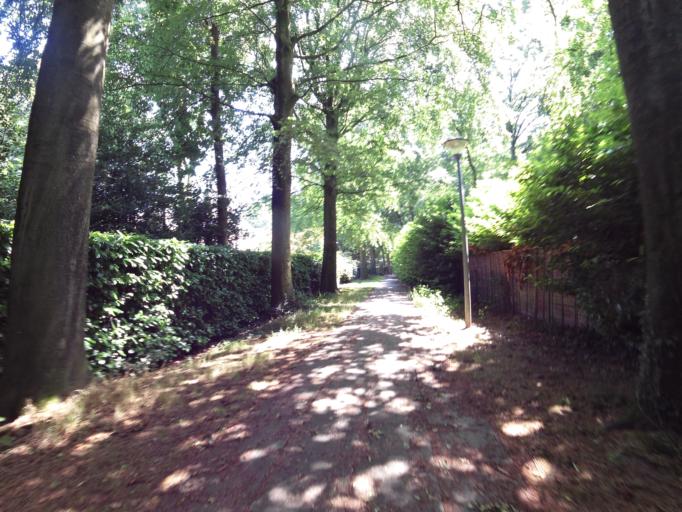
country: BE
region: Flanders
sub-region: Provincie West-Vlaanderen
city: Zedelgem
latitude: 51.1858
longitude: 3.1572
